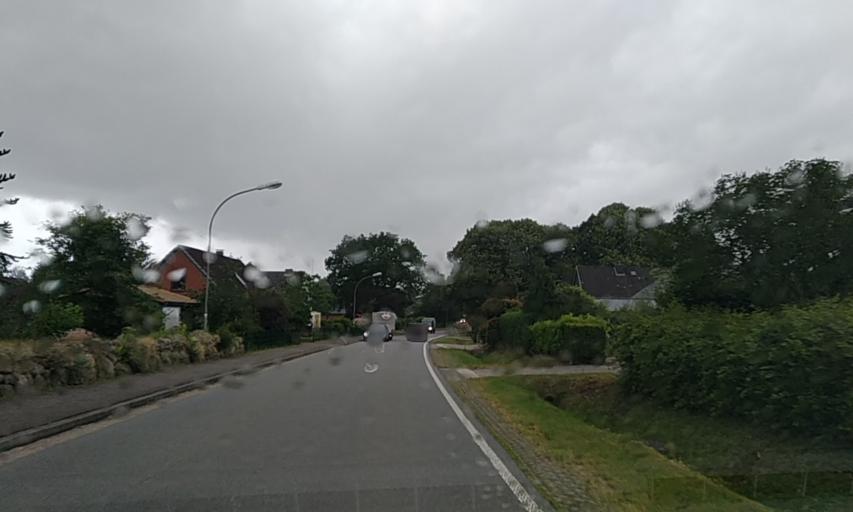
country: DE
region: Schleswig-Holstein
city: Neuberend
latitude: 54.5473
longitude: 9.5332
